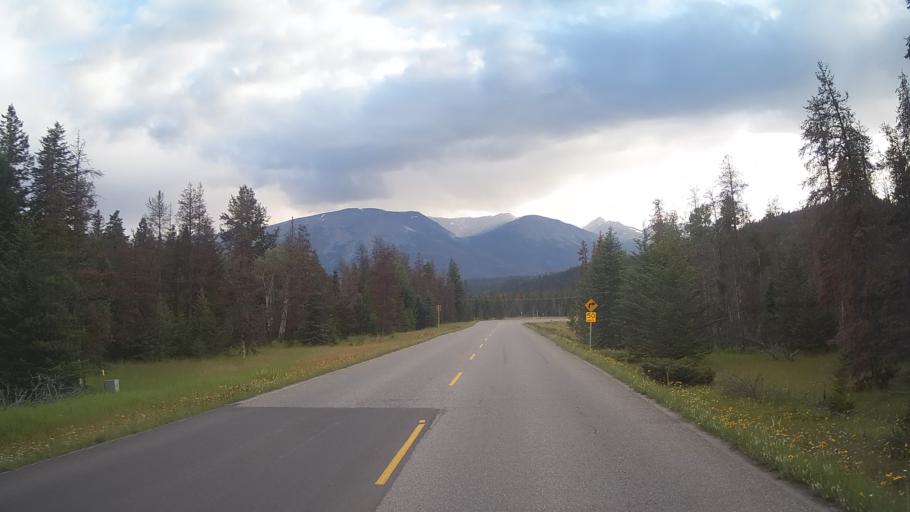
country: CA
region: Alberta
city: Jasper Park Lodge
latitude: 52.9114
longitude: -118.0529
